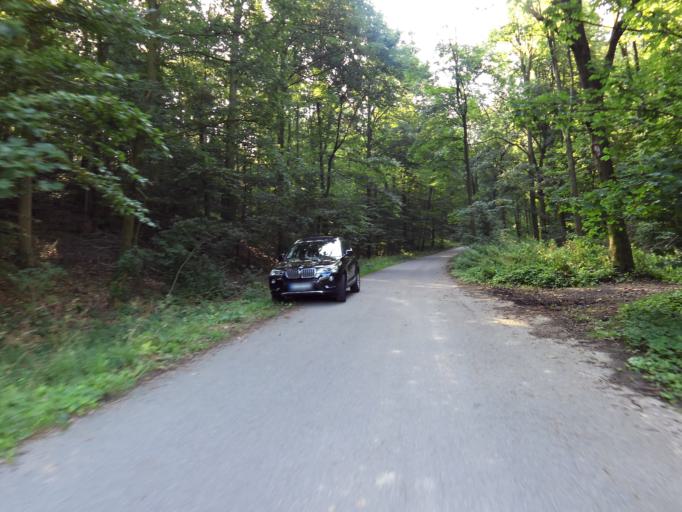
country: DE
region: North Rhine-Westphalia
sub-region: Regierungsbezirk Koln
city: Herzogenrath
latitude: 50.9070
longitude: 6.0874
